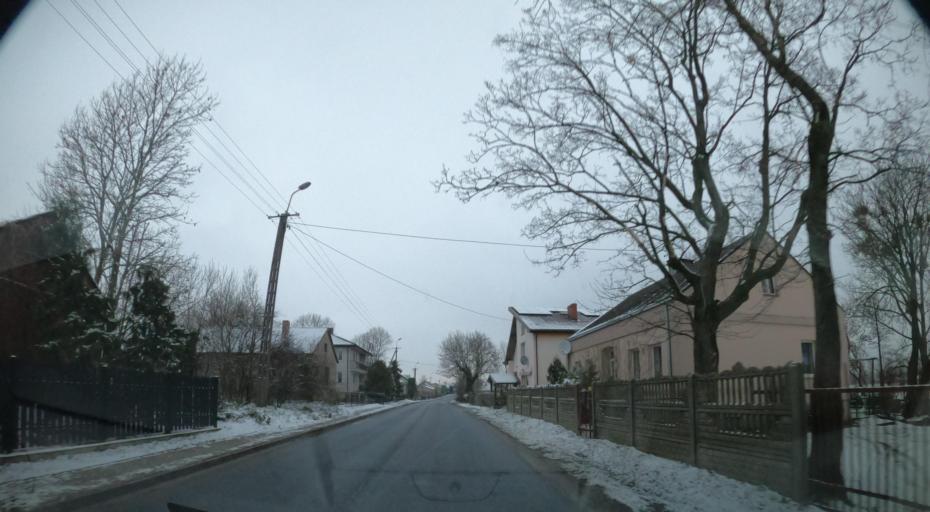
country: PL
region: Kujawsko-Pomorskie
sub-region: Powiat lipnowski
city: Wielgie
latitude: 52.6895
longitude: 19.2808
